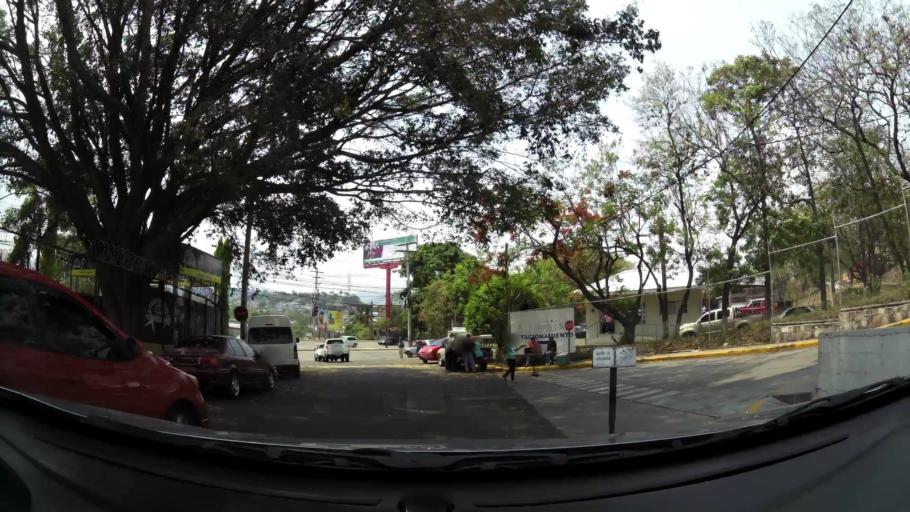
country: HN
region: Francisco Morazan
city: Tegucigalpa
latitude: 14.0636
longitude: -87.2187
